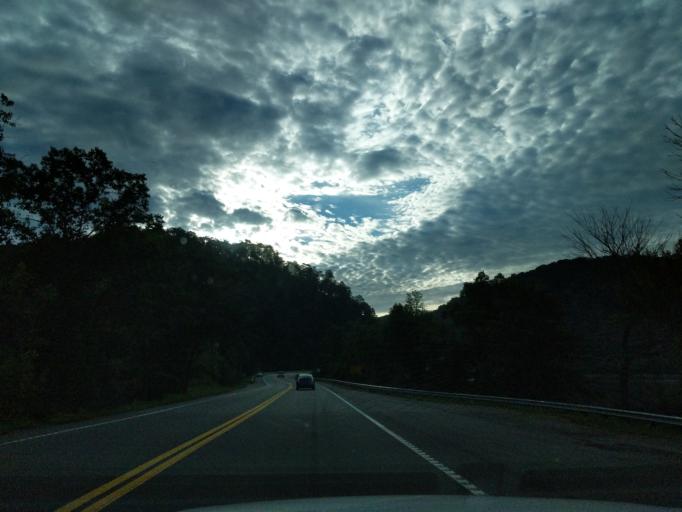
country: US
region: Tennessee
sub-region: Polk County
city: Benton
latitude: 35.1119
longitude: -84.5735
